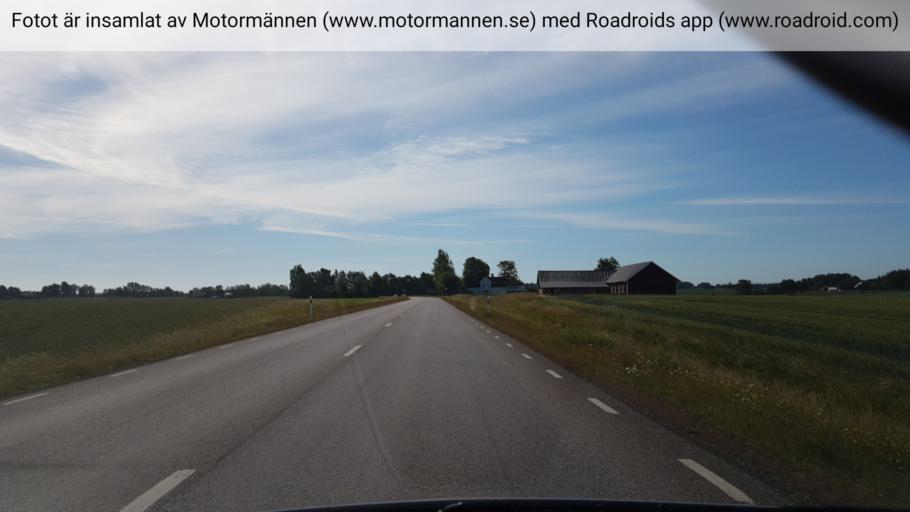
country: SE
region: Vaestra Goetaland
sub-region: Skovde Kommun
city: Skoevde
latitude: 58.3868
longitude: 13.9405
